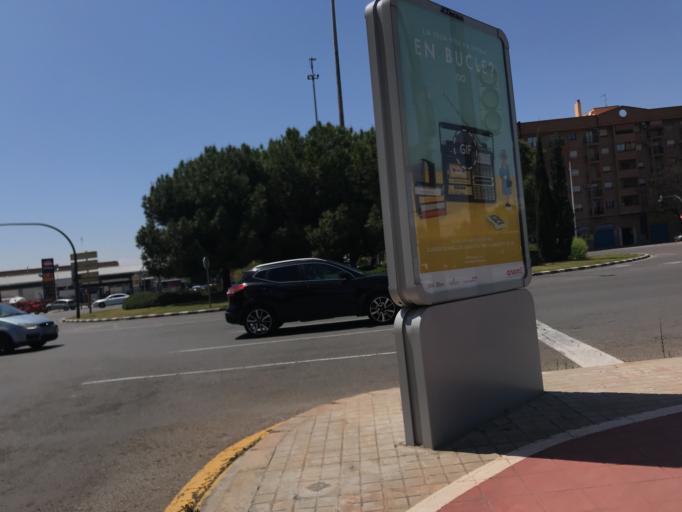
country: ES
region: Valencia
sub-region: Provincia de Valencia
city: Mislata
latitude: 39.4636
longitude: -0.4051
